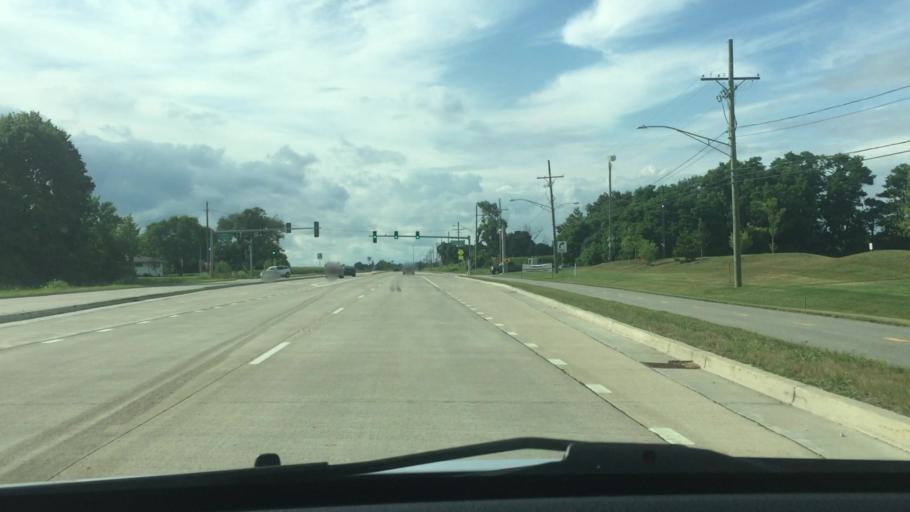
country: US
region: Illinois
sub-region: McHenry County
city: Lakewood
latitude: 42.2590
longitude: -88.3711
